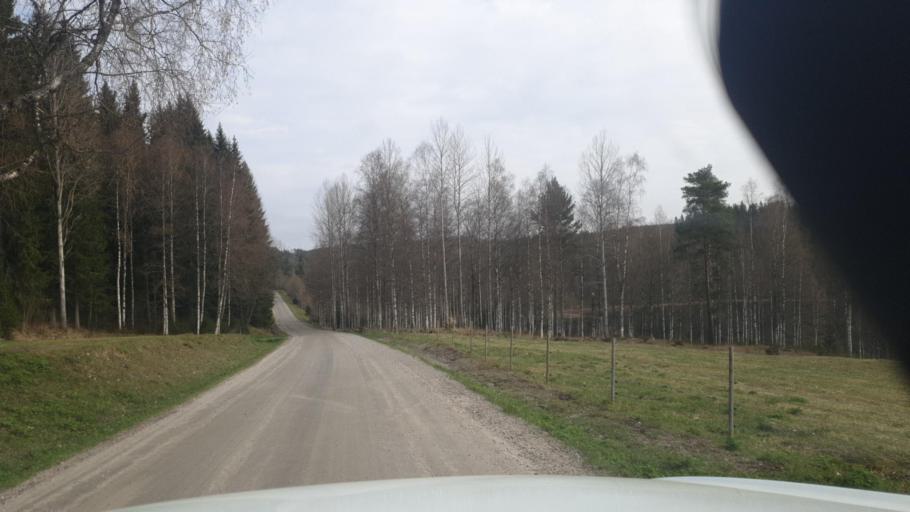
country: SE
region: Vaermland
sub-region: Arvika Kommun
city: Arvika
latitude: 59.8302
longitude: 12.7475
